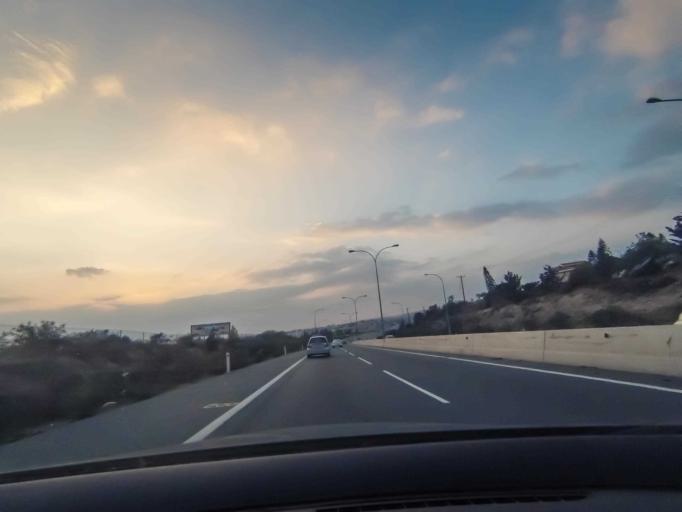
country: CY
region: Limassol
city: Mouttagiaka
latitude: 34.7061
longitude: 33.0973
